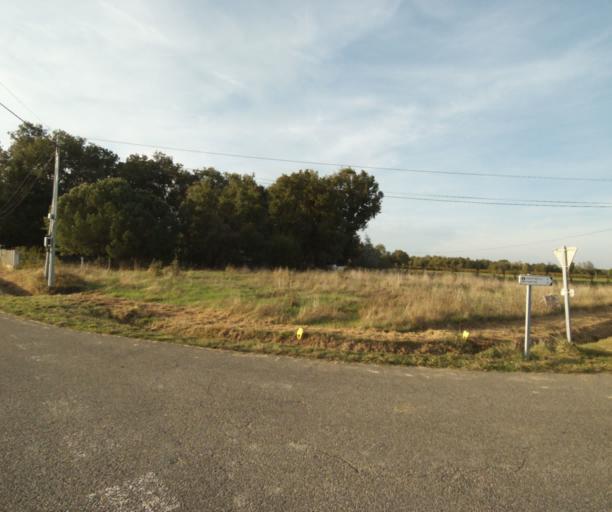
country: FR
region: Midi-Pyrenees
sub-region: Departement du Tarn-et-Garonne
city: Campsas
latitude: 43.8895
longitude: 1.3455
